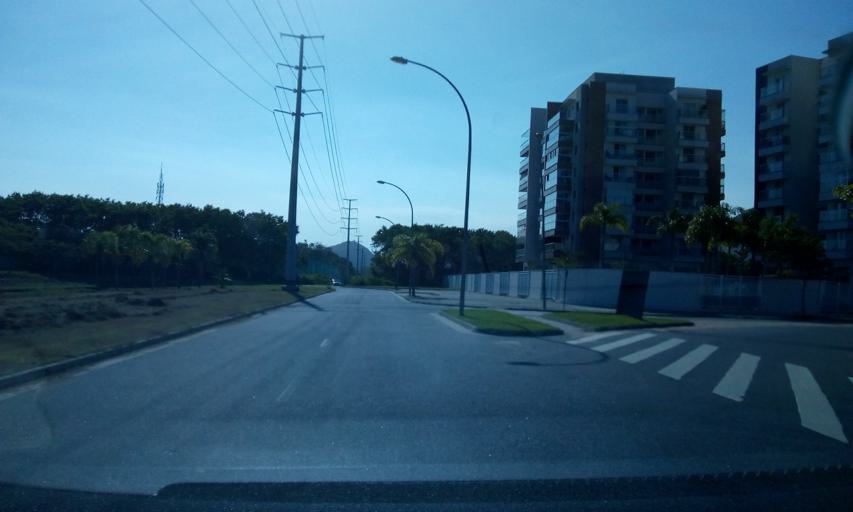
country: BR
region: Rio de Janeiro
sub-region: Nilopolis
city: Nilopolis
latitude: -22.9942
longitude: -43.4019
